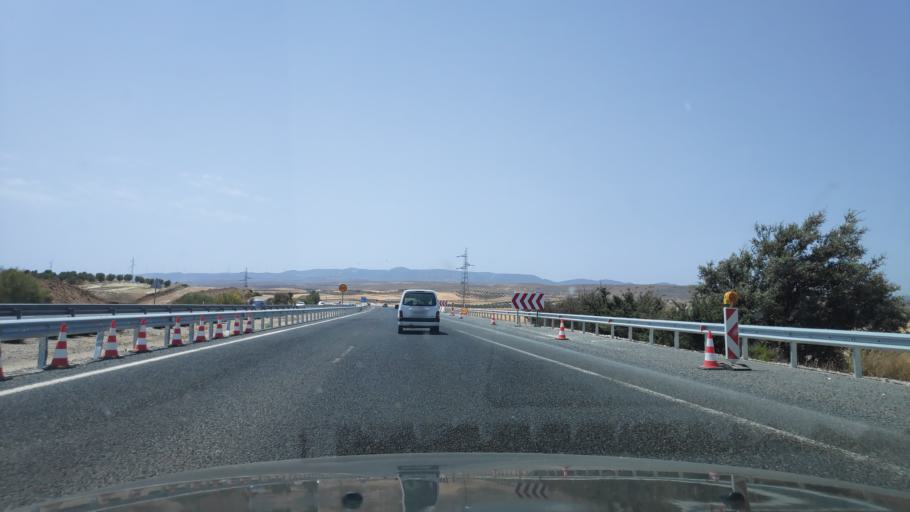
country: ES
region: Andalusia
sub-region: Provincia de Granada
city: Otura
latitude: 37.0641
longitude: -3.6534
